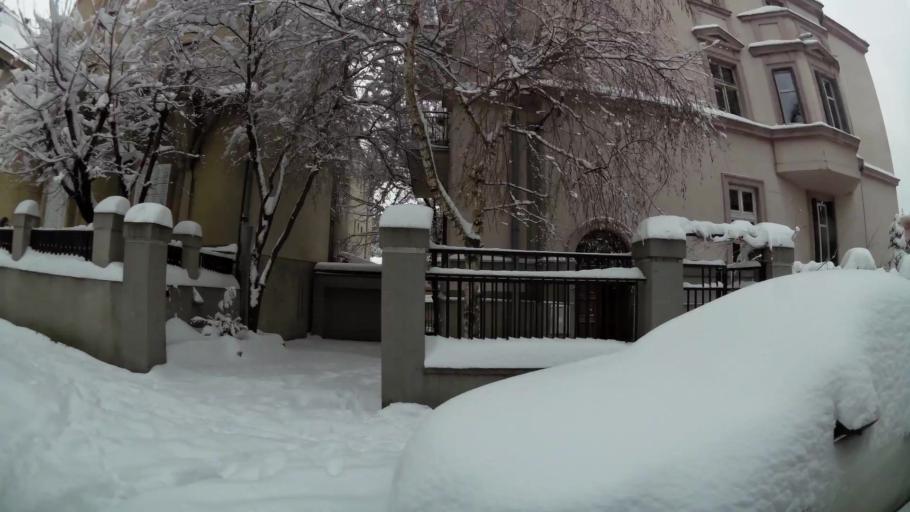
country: RS
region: Central Serbia
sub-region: Belgrade
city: Vracar
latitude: 44.7961
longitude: 20.4685
